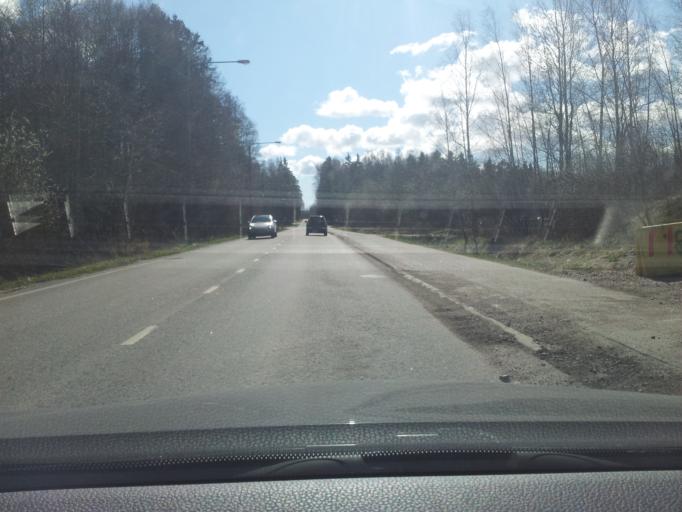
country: FI
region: Uusimaa
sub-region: Helsinki
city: Koukkuniemi
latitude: 60.1523
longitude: 24.7080
